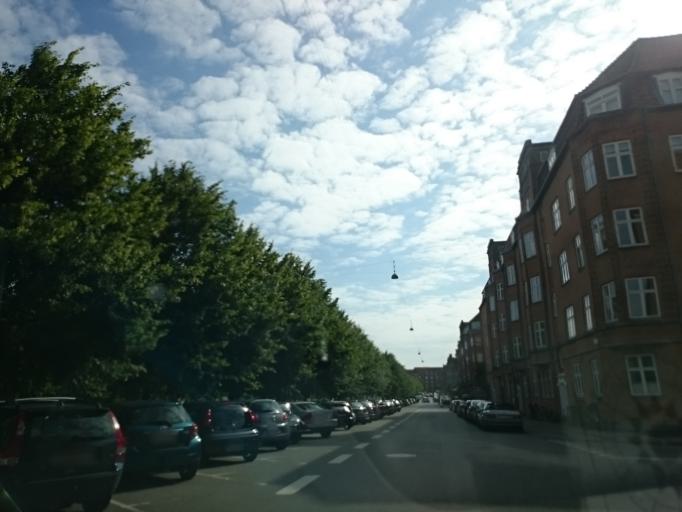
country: DK
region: Central Jutland
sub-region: Arhus Kommune
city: Arhus
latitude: 56.1441
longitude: 10.1923
